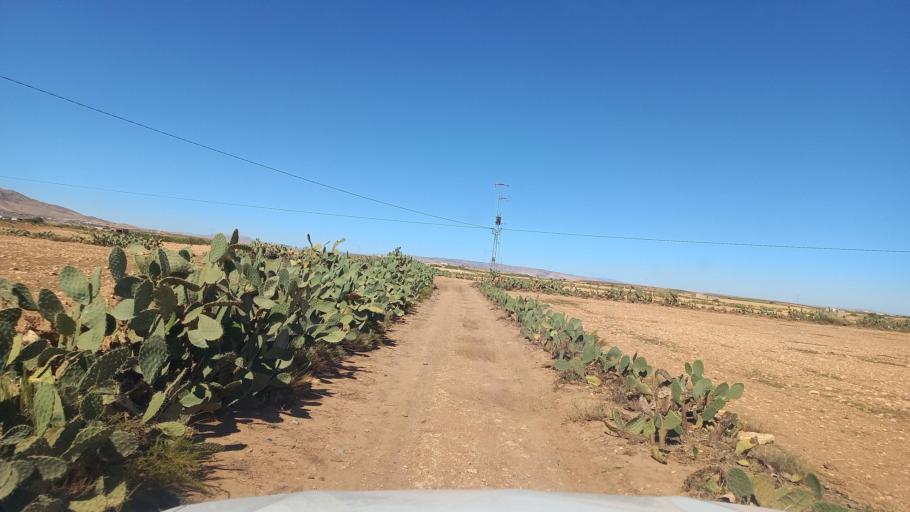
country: TN
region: Al Qasrayn
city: Sbiba
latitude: 35.3836
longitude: 9.0918
